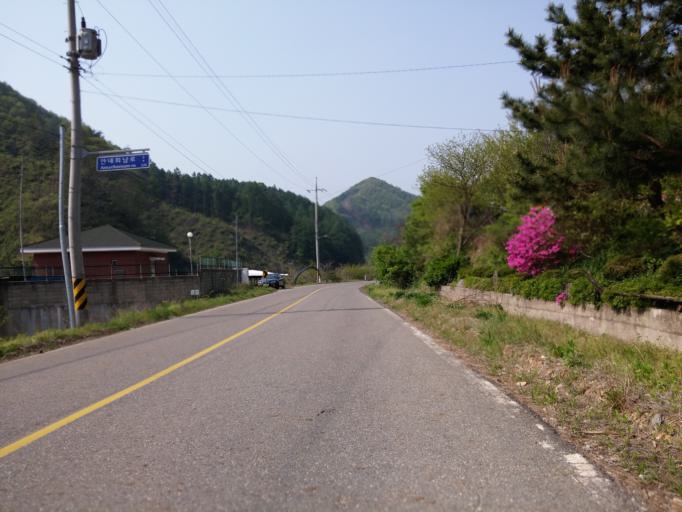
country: KR
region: Chungcheongbuk-do
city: Okcheon
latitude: 36.4109
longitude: 127.6246
